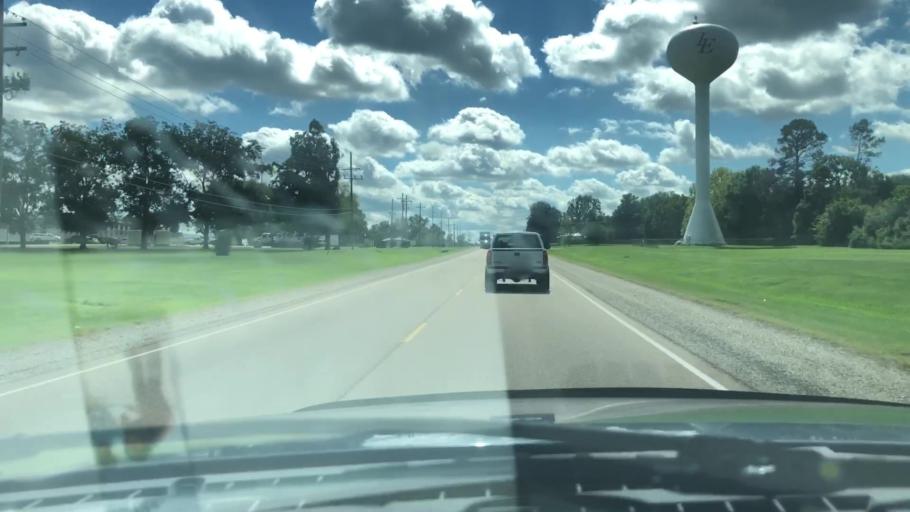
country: US
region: Texas
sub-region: Bowie County
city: Wake Village
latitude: 33.3791
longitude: -94.0922
